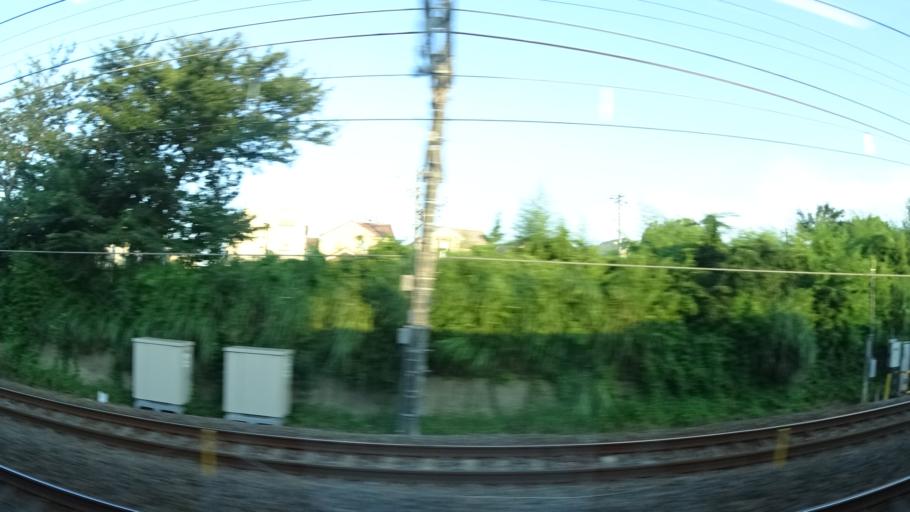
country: JP
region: Chiba
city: Abiko
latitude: 35.8734
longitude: 140.0476
